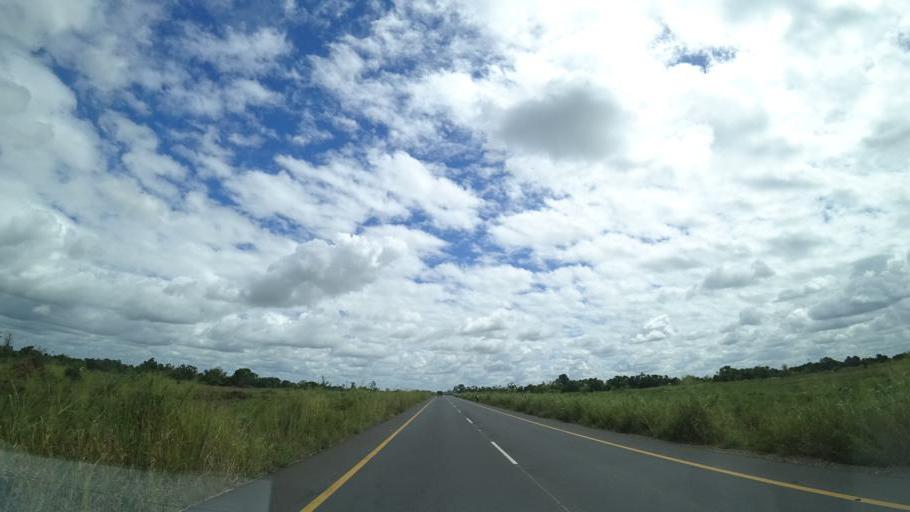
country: MZ
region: Sofala
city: Dondo
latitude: -19.3917
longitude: 34.4187
